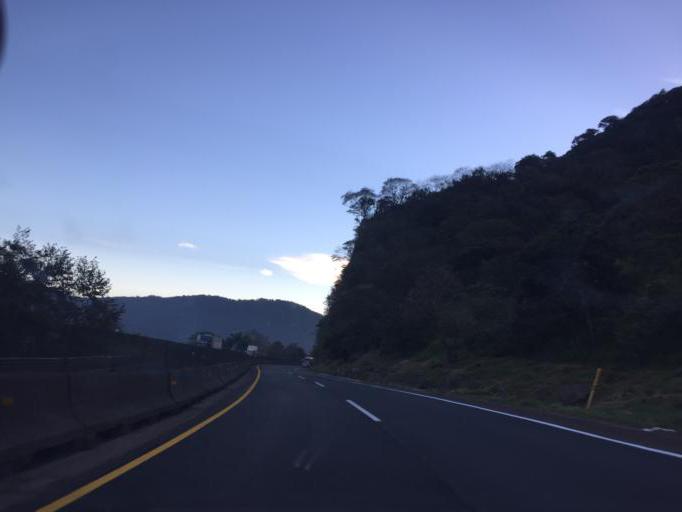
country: MX
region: Veracruz
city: Rio Blanco
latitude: 18.8329
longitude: -97.1404
